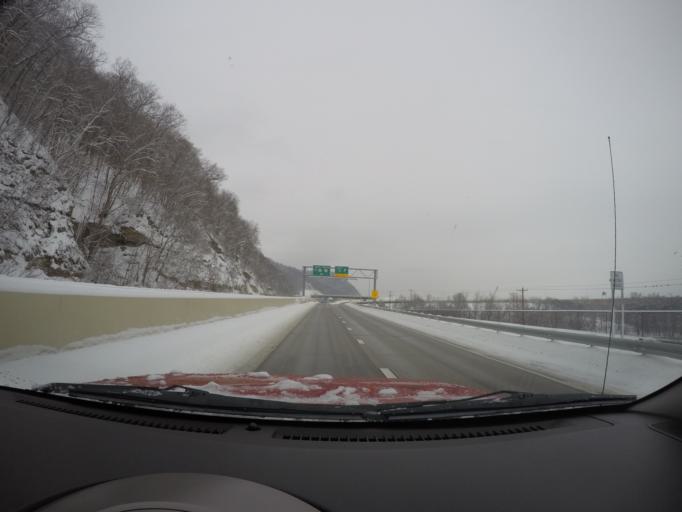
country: US
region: Minnesota
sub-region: Houston County
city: La Crescent
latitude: 43.8542
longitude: -91.3022
